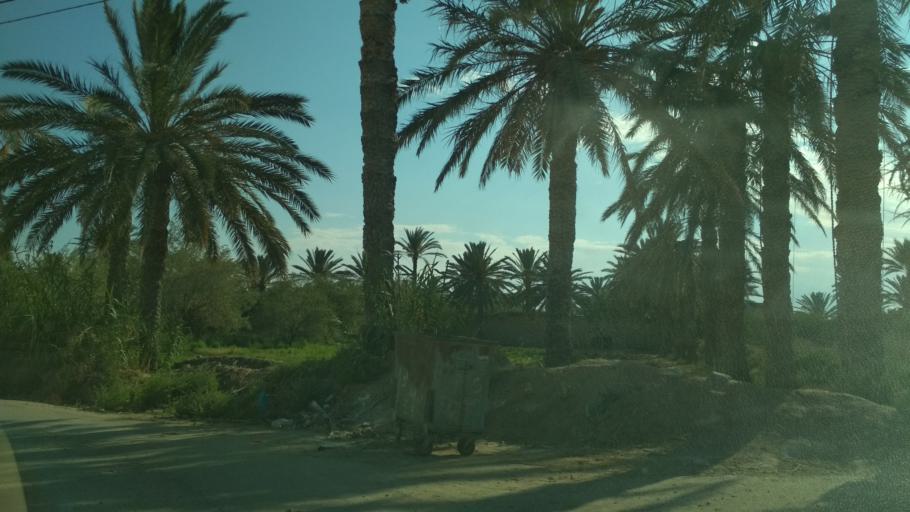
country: TN
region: Qabis
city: Gabes
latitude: 33.9484
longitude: 10.0635
